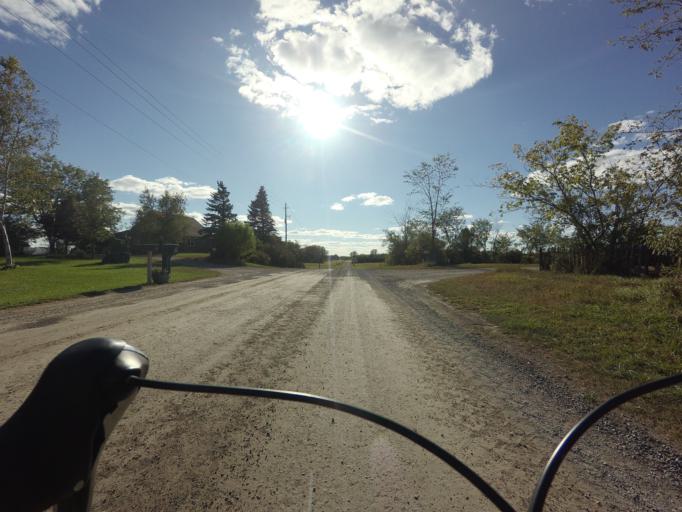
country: CA
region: Ontario
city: Bells Corners
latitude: 45.1116
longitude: -75.7142
